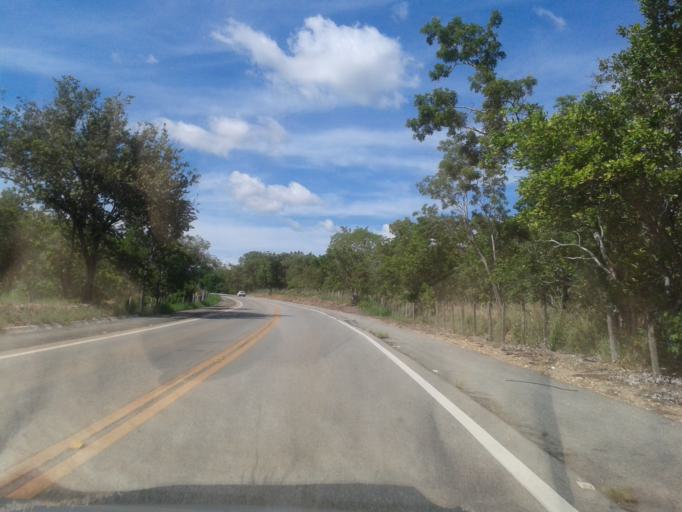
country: BR
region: Goias
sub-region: Itapuranga
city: Itapuranga
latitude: -15.3756
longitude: -50.3875
